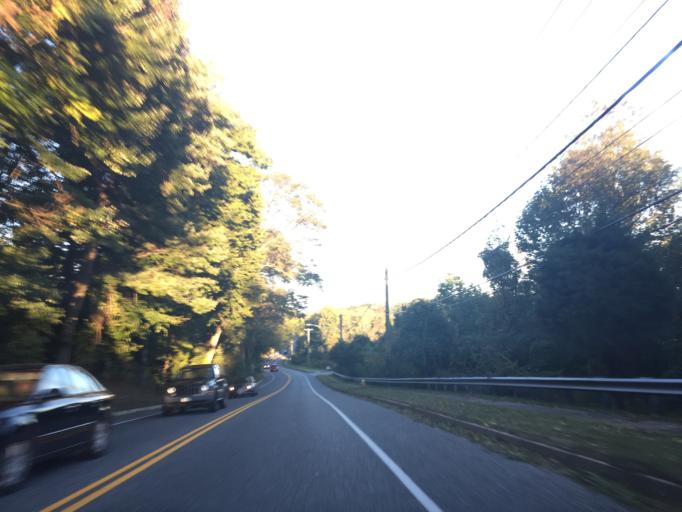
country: US
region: Maryland
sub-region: Harford County
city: Bel Air South
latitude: 39.4783
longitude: -76.3259
